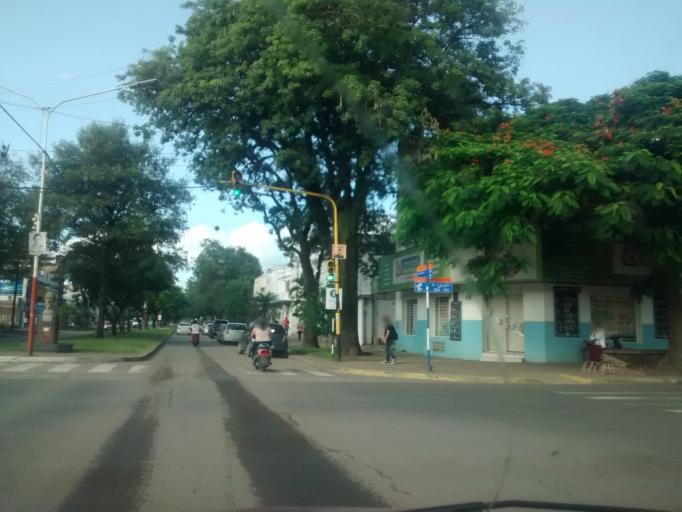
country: AR
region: Chaco
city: Resistencia
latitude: -27.4550
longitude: -58.9821
